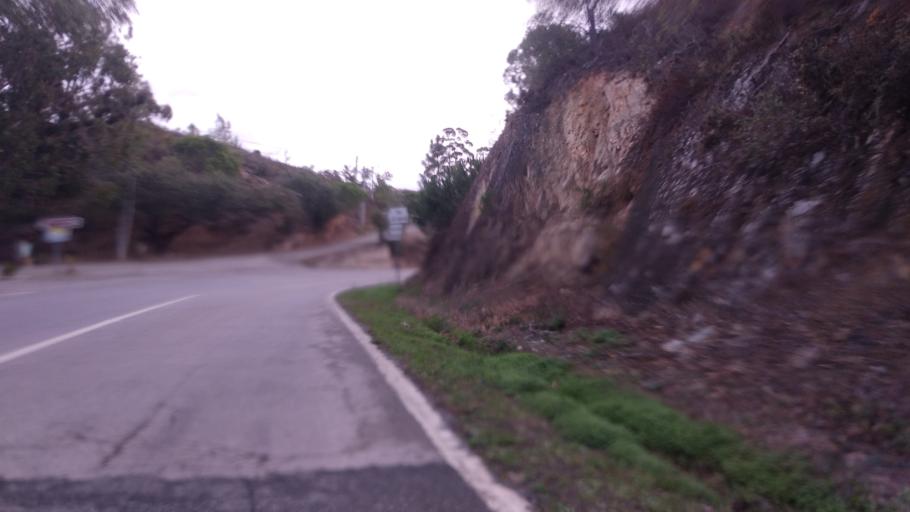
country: PT
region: Faro
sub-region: Sao Bras de Alportel
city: Sao Bras de Alportel
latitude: 37.1799
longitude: -7.9110
